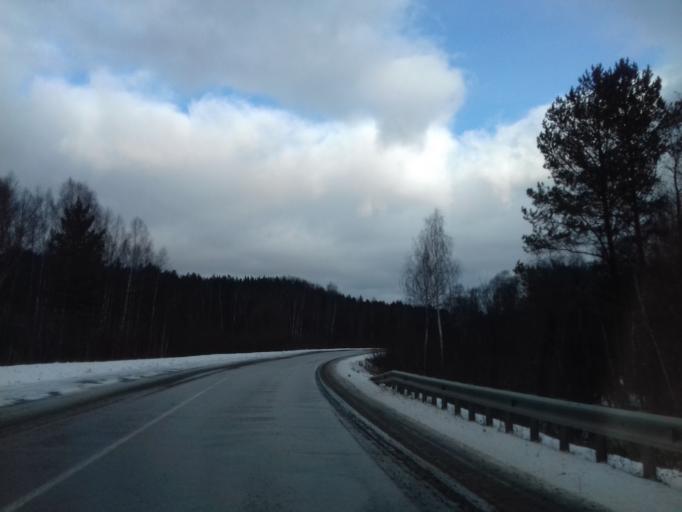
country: RU
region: Bashkortostan
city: Lomovka
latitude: 53.8165
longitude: 57.9636
